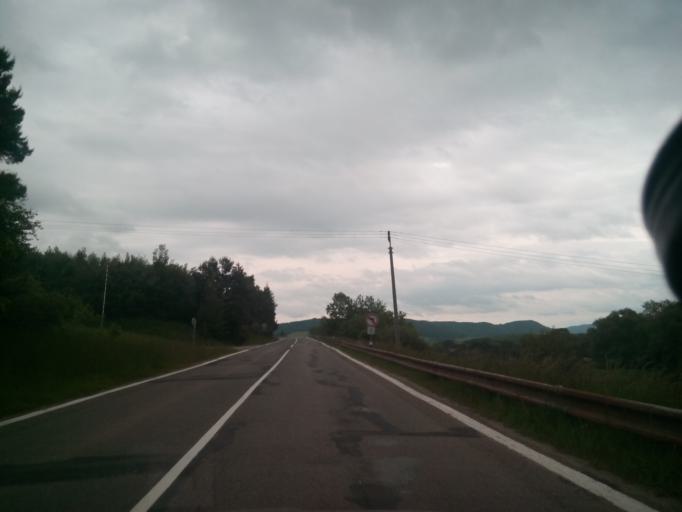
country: SK
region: Kosicky
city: Krompachy
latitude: 48.9952
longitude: 20.9052
